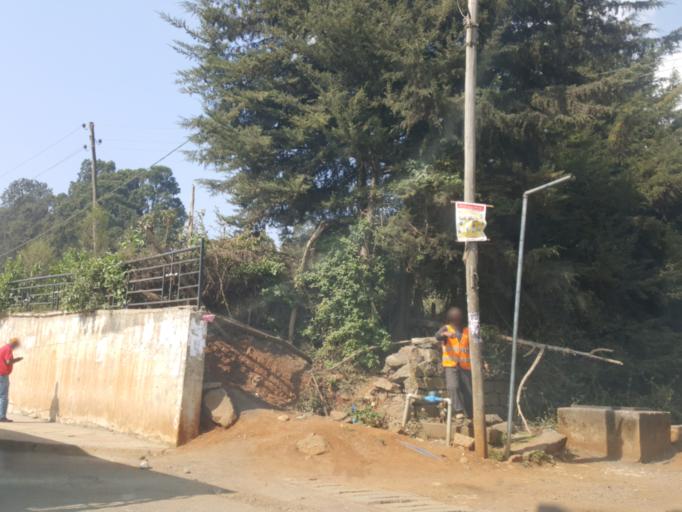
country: ET
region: Adis Abeba
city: Addis Ababa
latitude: 9.0557
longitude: 38.7164
